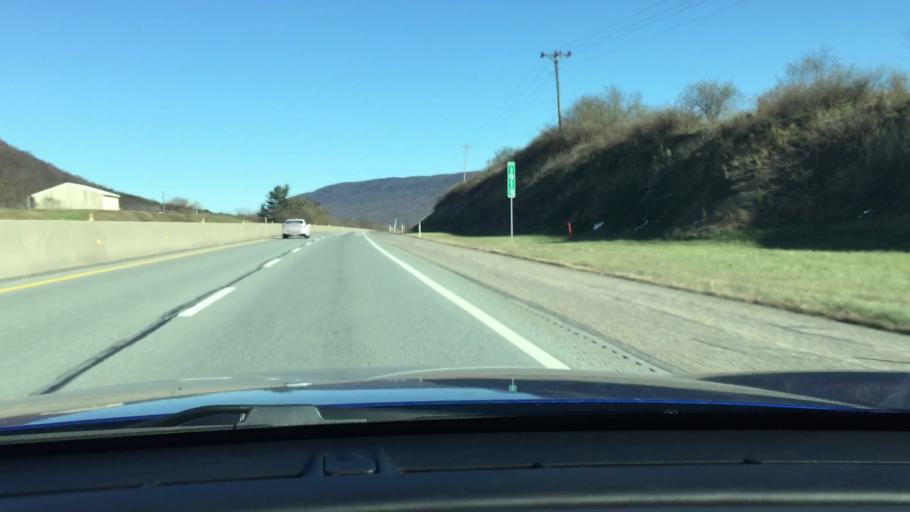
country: US
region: Pennsylvania
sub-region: Franklin County
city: Doylestown
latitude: 40.1234
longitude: -77.7725
